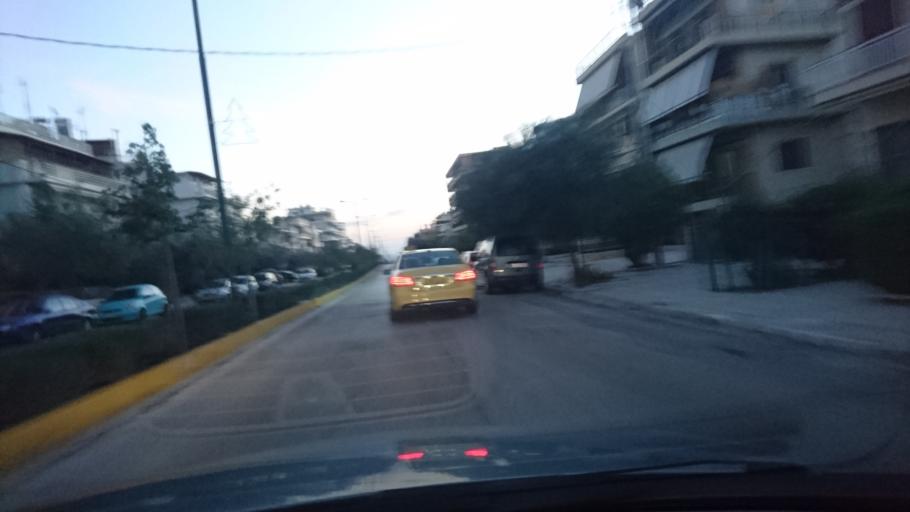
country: GR
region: Attica
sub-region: Nomarchia Athinas
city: Argyroupoli
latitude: 37.9227
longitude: 23.7504
